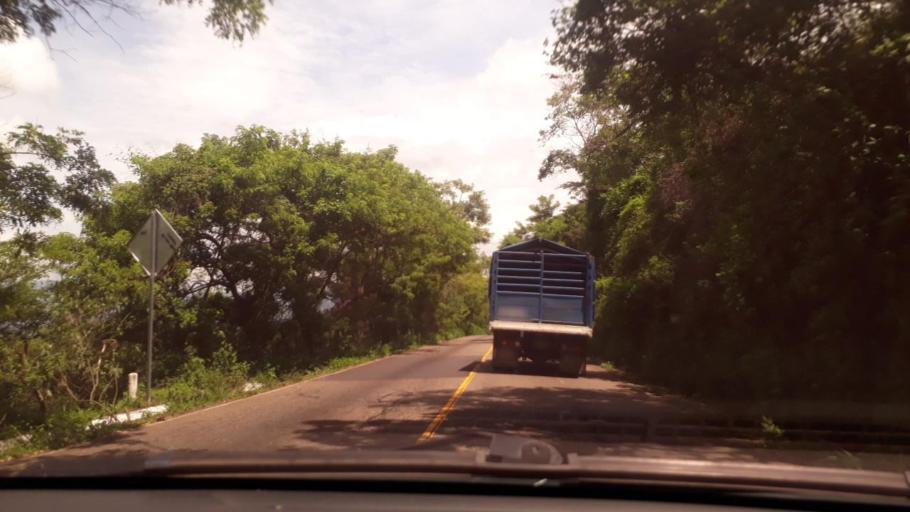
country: GT
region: Jutiapa
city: Jalpatagua
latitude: 14.1766
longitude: -90.0465
